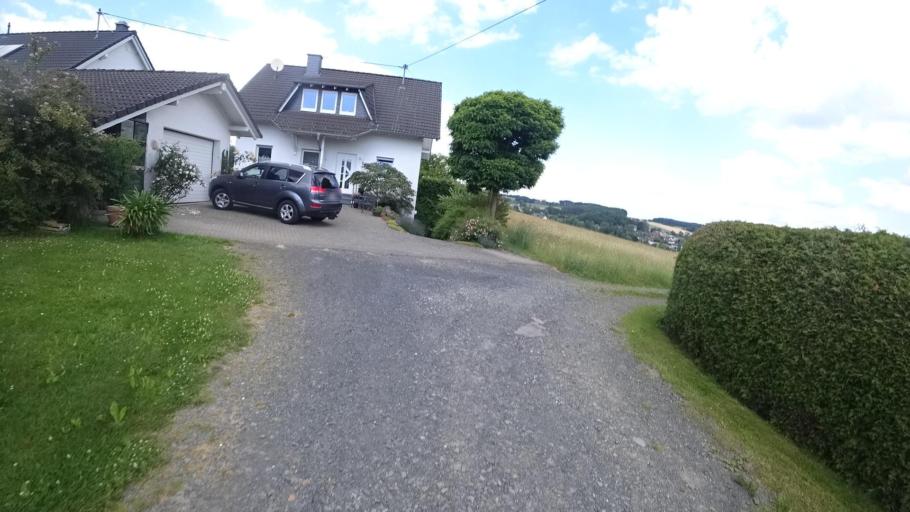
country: DE
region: Rheinland-Pfalz
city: Busenhausen
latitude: 50.7102
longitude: 7.6296
